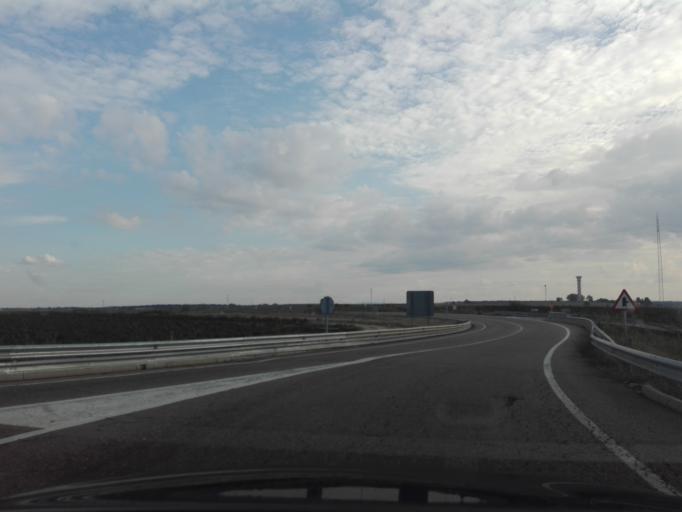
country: ES
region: Extremadura
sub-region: Provincia de Badajoz
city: Valdelacalzada
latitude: 38.8499
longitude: -6.7132
